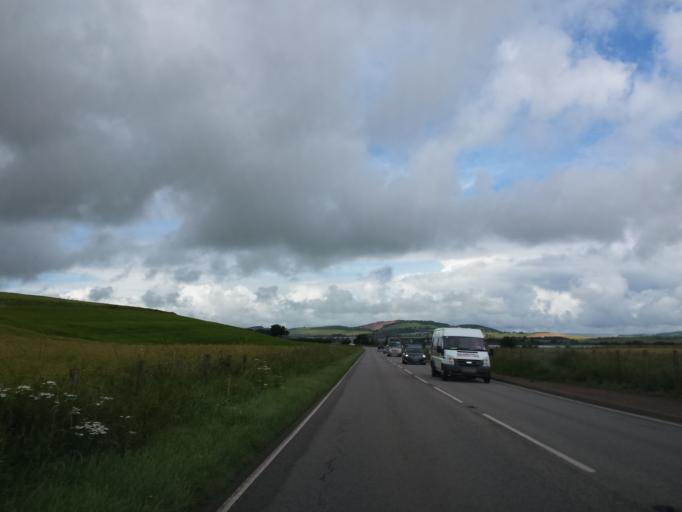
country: GB
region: Scotland
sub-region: Fife
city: Strathkinness
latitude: 56.3577
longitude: -2.8638
